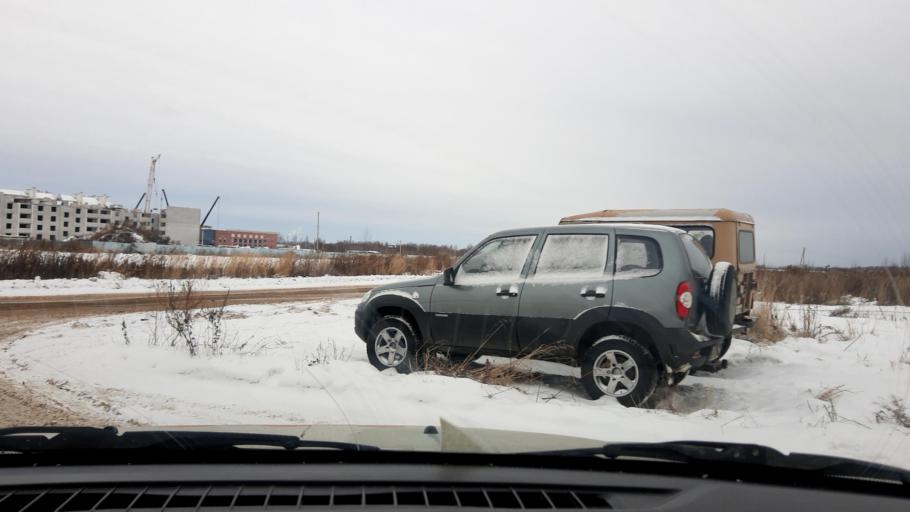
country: RU
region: Nizjnij Novgorod
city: Gorodets
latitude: 56.6689
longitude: 43.4768
